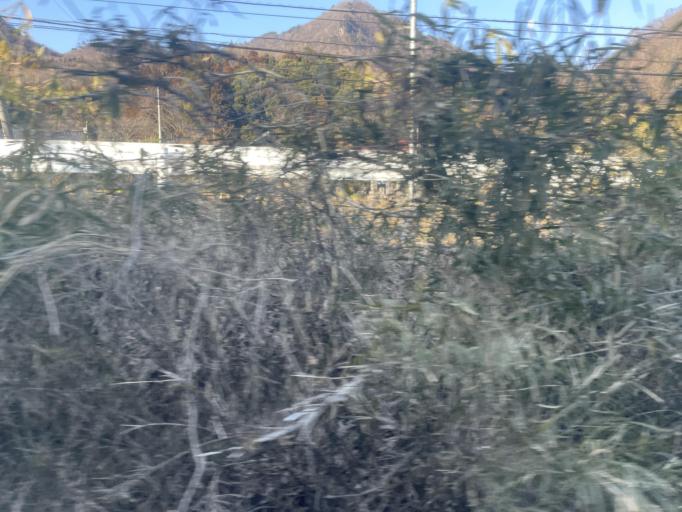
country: JP
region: Gunma
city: Nakanojomachi
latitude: 36.5666
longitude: 138.8897
